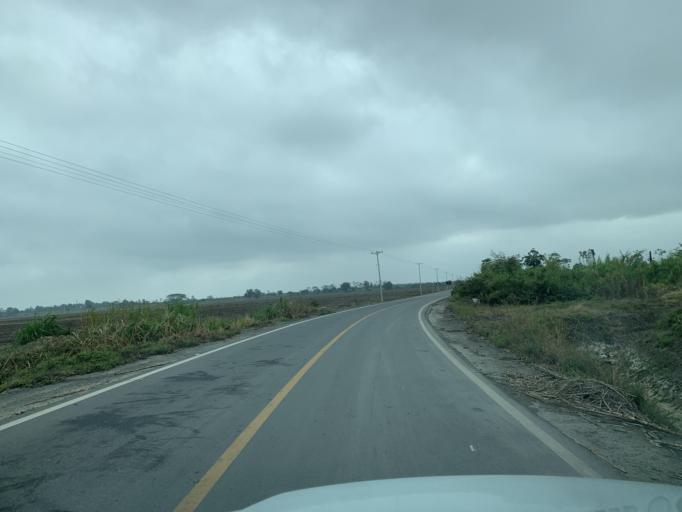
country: EC
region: Guayas
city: Coronel Marcelino Mariduena
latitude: -2.3083
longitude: -79.5090
